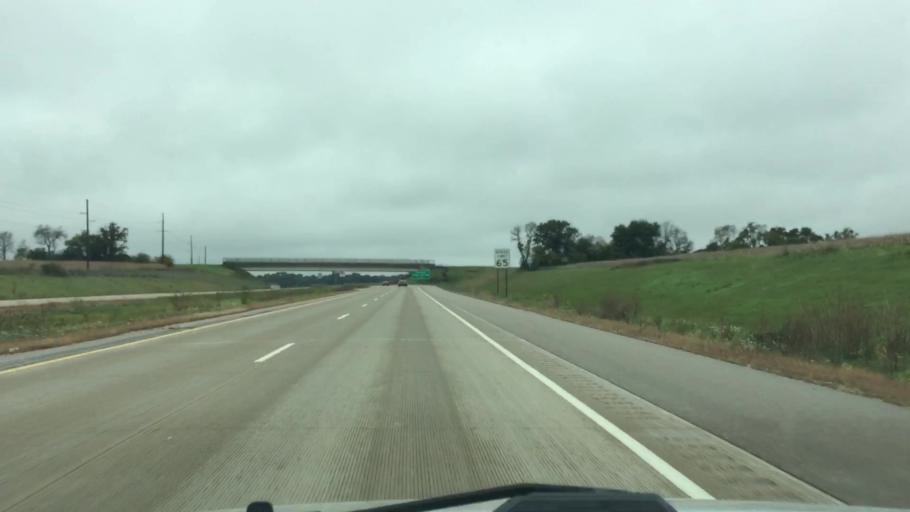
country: US
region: Wisconsin
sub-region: Rock County
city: Milton
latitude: 42.7622
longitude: -88.9325
